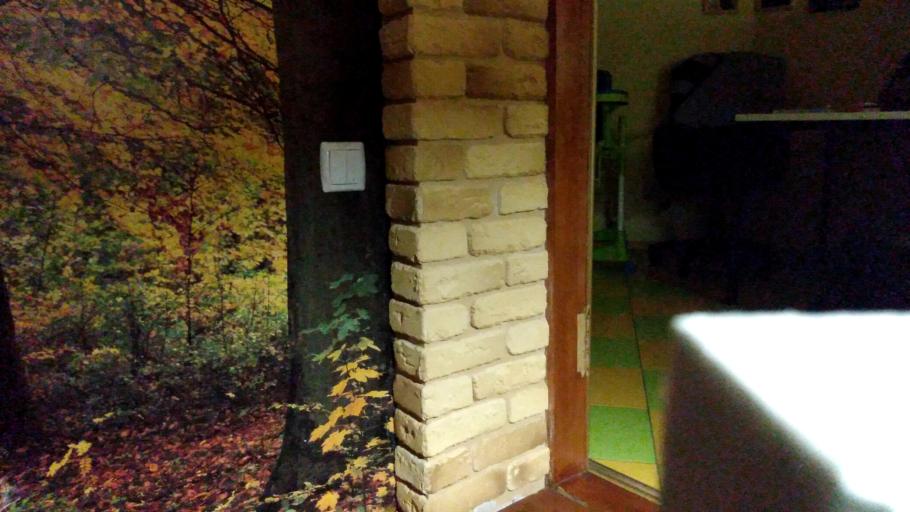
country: RU
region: Vologda
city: Lipin Bor
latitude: 60.8992
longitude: 37.9973
